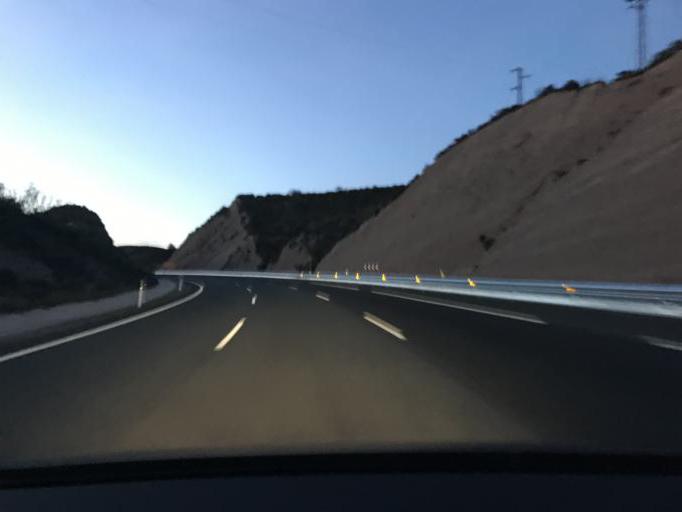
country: ES
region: Andalusia
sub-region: Provincia de Granada
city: Lanjaron
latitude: 36.9124
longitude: -3.5273
